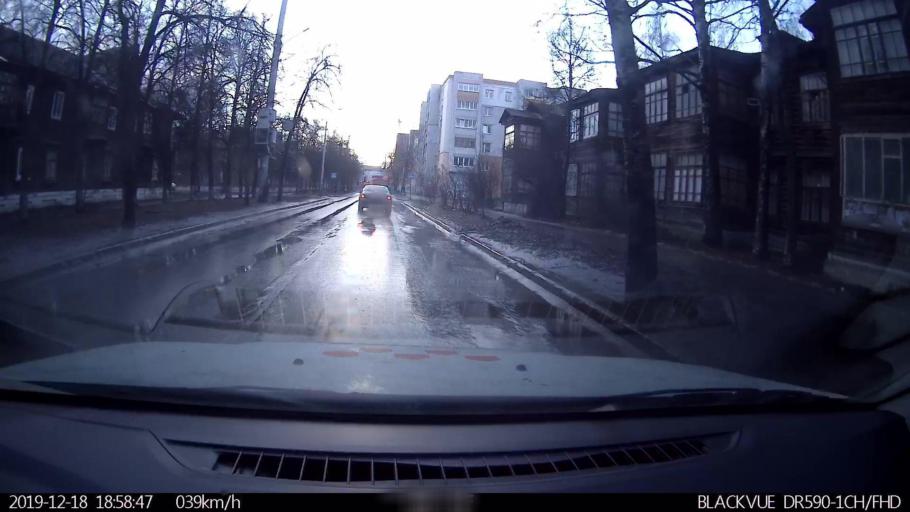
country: RU
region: Nizjnij Novgorod
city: Gorbatovka
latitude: 56.3337
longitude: 43.8399
